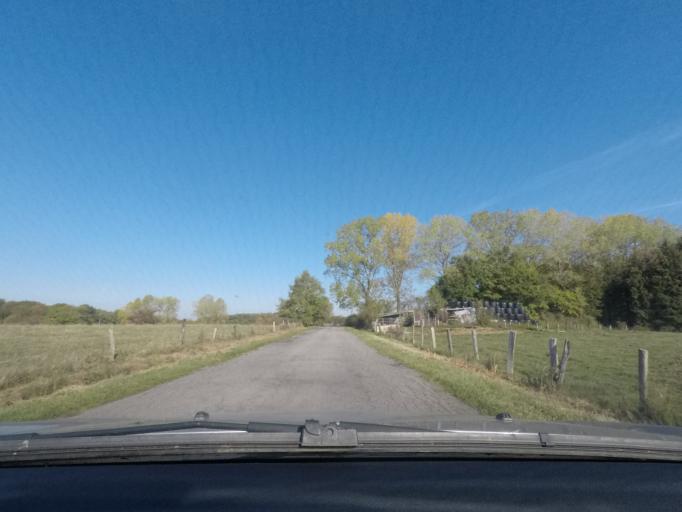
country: BE
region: Wallonia
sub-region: Province du Luxembourg
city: Etalle
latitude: 49.6982
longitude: 5.5707
